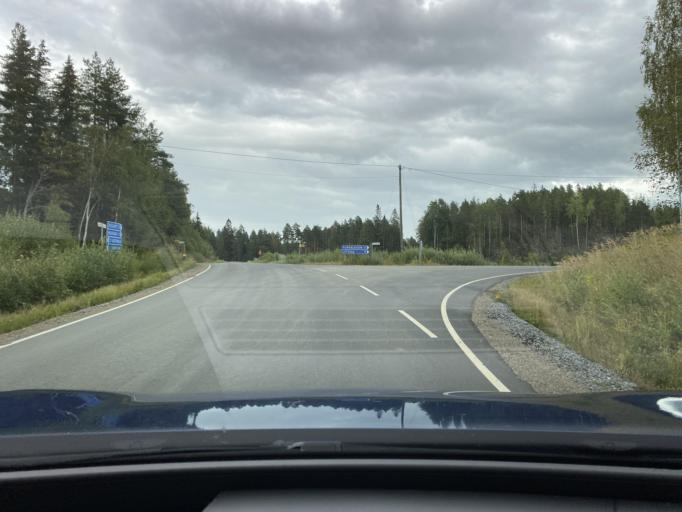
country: FI
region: Pirkanmaa
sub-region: Lounais-Pirkanmaa
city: Punkalaidun
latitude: 61.2324
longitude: 23.1473
